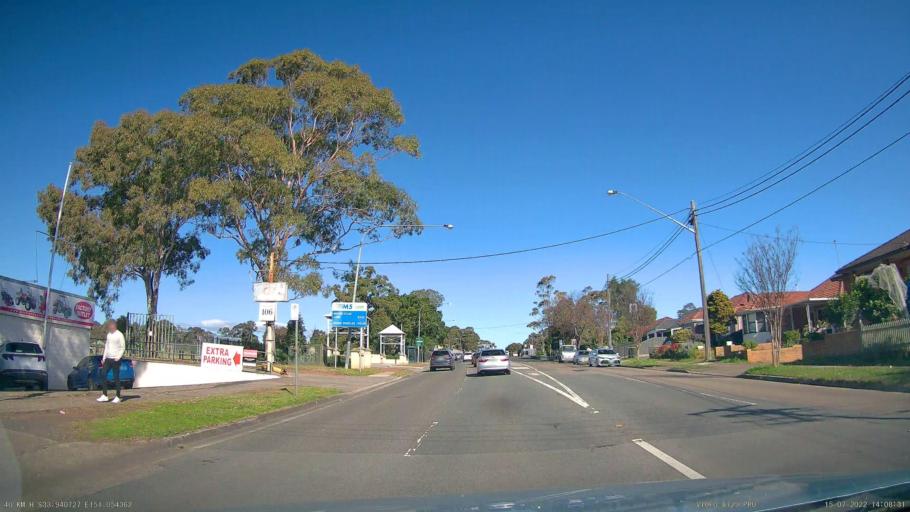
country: AU
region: New South Wales
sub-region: Canterbury
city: Roselands
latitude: -33.9409
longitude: 151.0543
